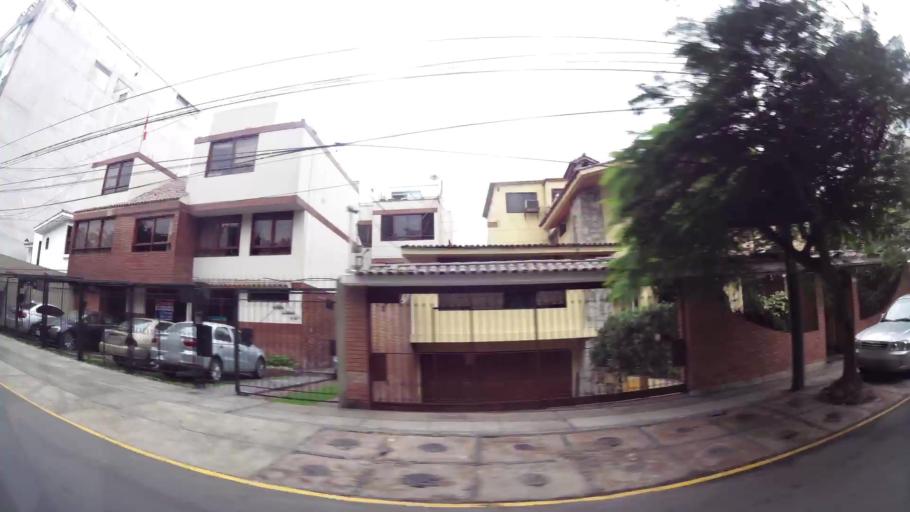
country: PE
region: Lima
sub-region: Lima
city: San Luis
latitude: -12.0939
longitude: -76.9877
